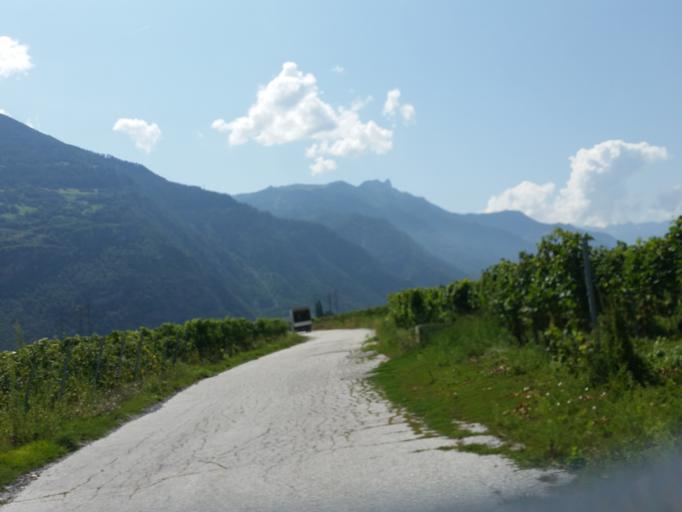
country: CH
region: Valais
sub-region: Conthey District
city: Ardon
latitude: 46.2022
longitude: 7.2538
